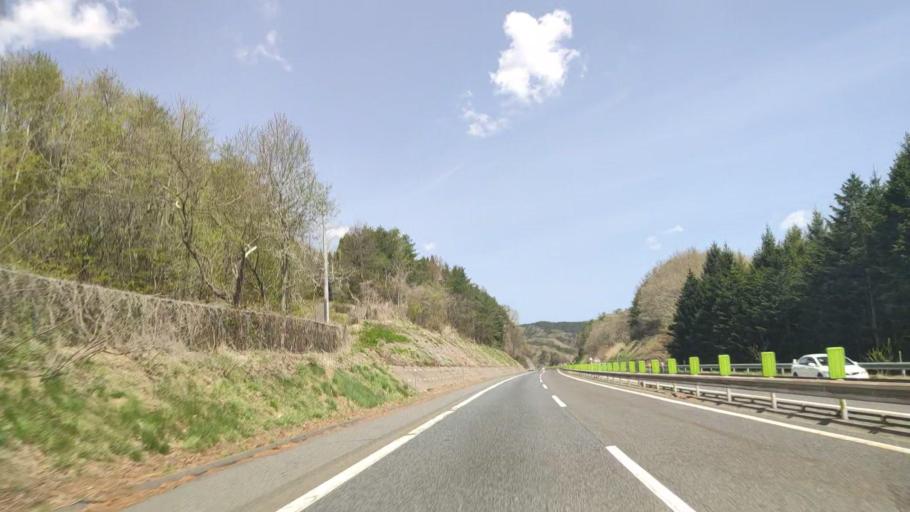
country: JP
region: Aomori
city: Hachinohe
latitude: 40.3527
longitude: 141.4483
